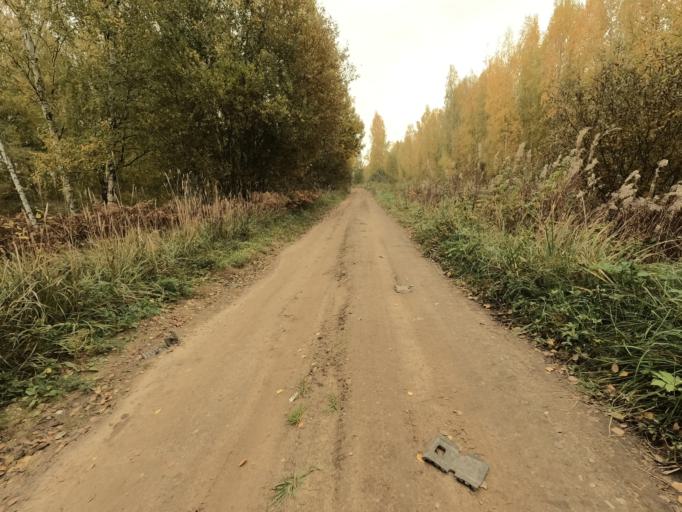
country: RU
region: Novgorod
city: Pankovka
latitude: 58.8656
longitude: 30.9279
